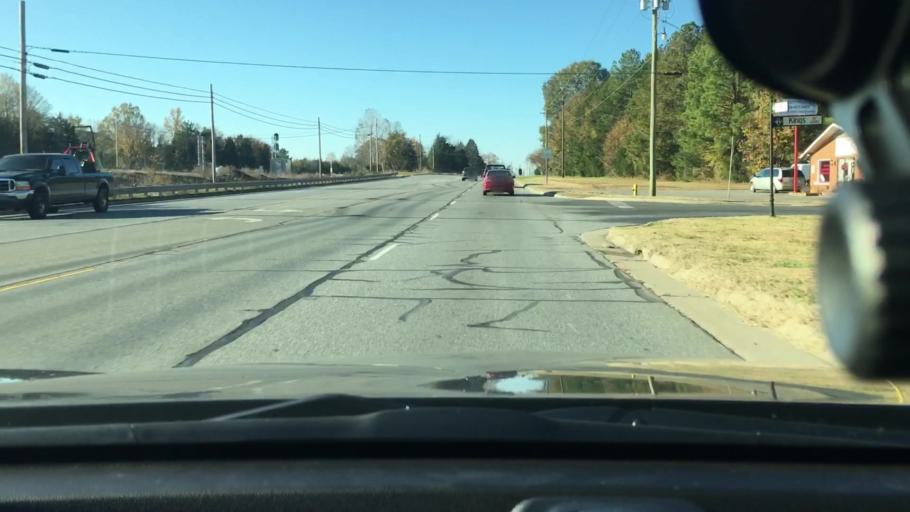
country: US
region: North Carolina
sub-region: Cabarrus County
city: Harrisburg
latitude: 35.3271
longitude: -80.6356
